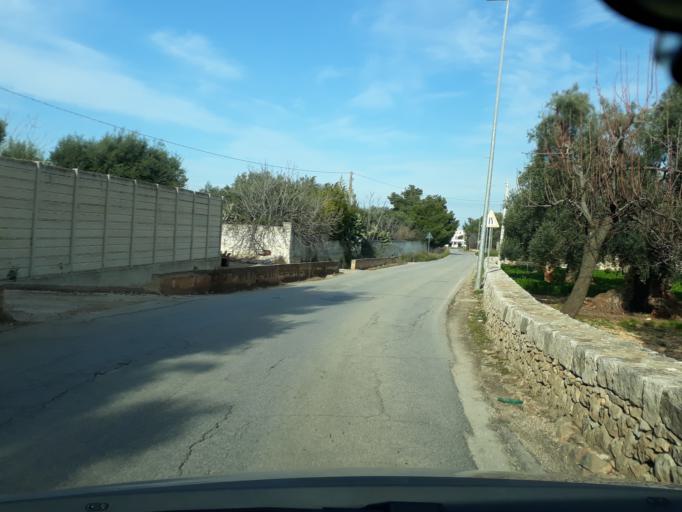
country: IT
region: Apulia
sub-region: Provincia di Brindisi
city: Fasano
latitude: 40.8245
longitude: 17.3595
